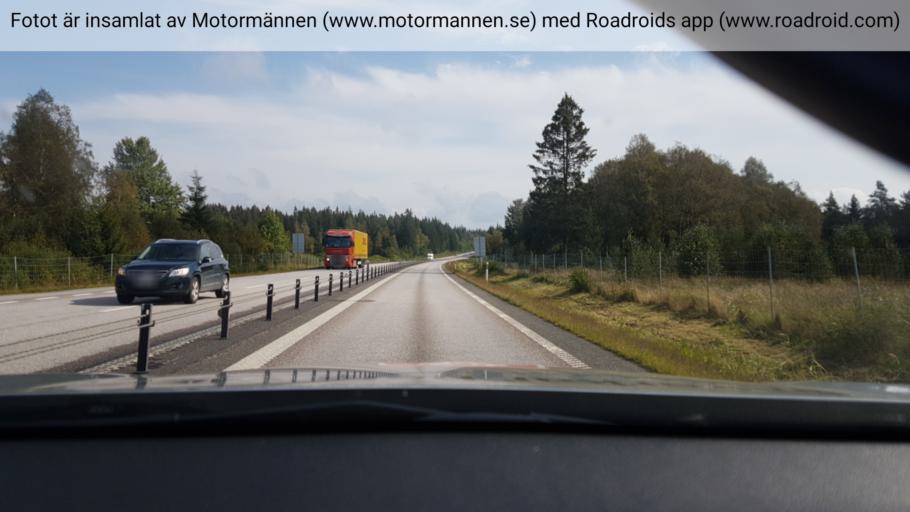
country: SE
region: Vaestra Goetaland
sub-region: Ulricehamns Kommun
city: Ulricehamn
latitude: 57.7971
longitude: 13.6027
